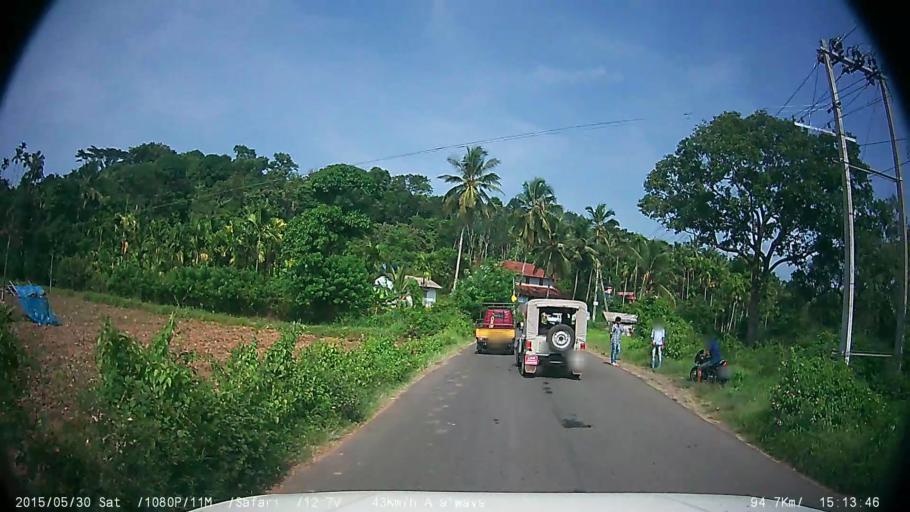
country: IN
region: Kerala
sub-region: Wayanad
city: Panamaram
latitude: 11.7893
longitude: 76.0442
